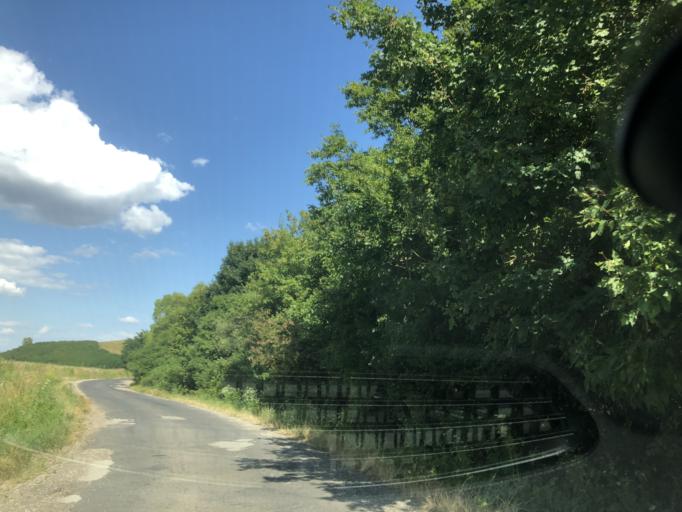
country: HU
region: Borsod-Abauj-Zemplen
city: Szendro
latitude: 48.5421
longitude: 20.7940
